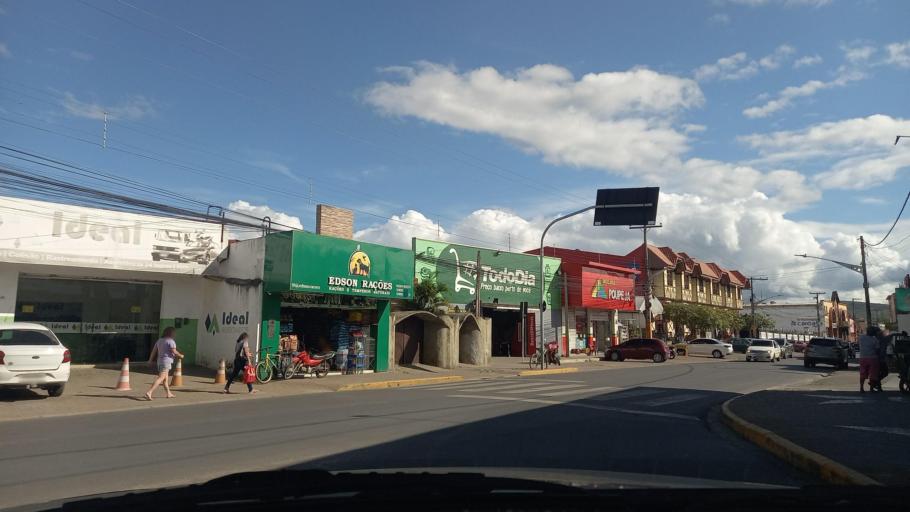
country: BR
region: Pernambuco
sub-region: Gravata
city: Gravata
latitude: -8.1978
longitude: -35.5608
